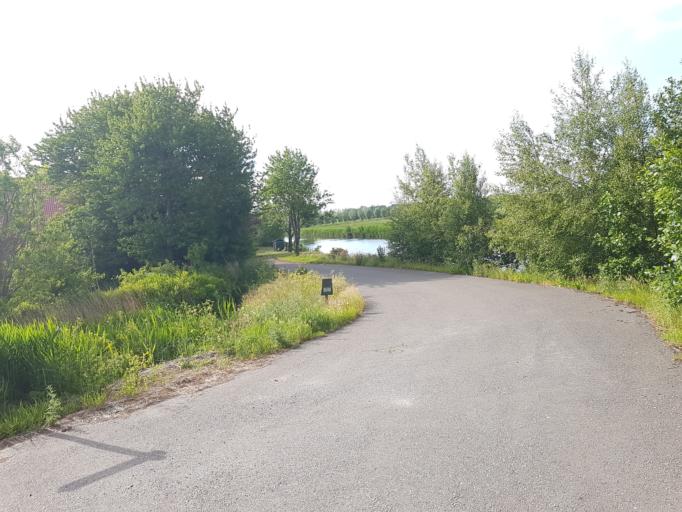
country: NL
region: Friesland
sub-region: Gemeente Smallingerland
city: Oudega
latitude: 53.0928
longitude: 5.9607
